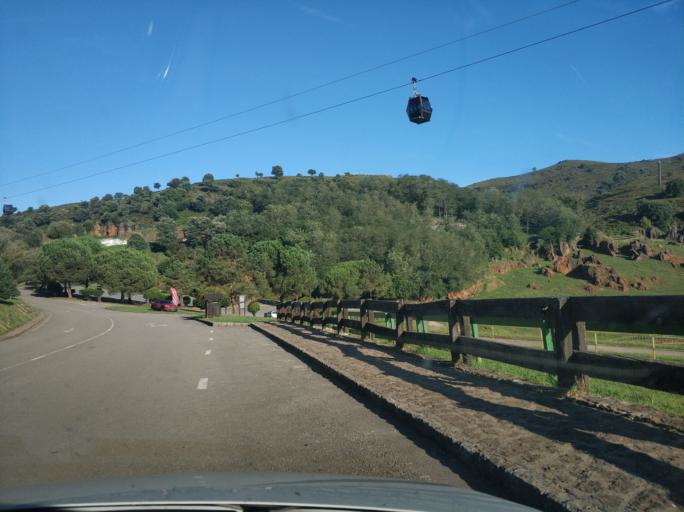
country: ES
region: Cantabria
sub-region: Provincia de Cantabria
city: Penagos
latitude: 43.3595
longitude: -3.8242
